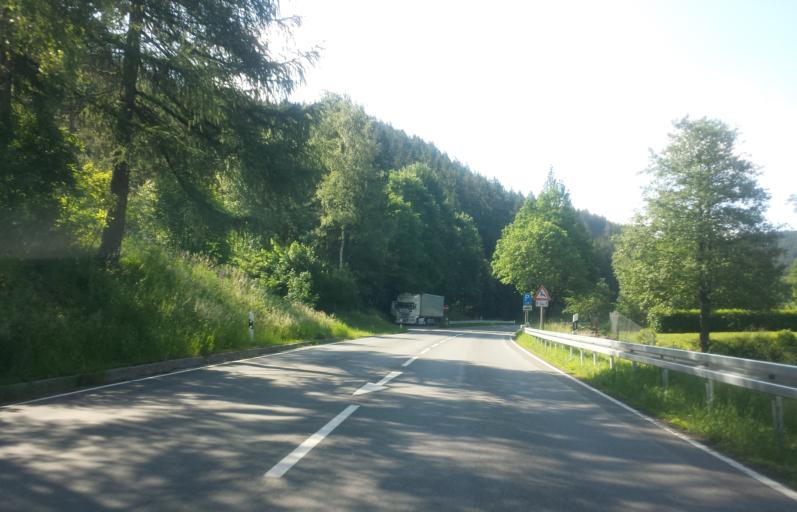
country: DE
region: Bavaria
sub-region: Upper Franconia
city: Ludwigsstadt
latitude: 50.4786
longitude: 11.3940
